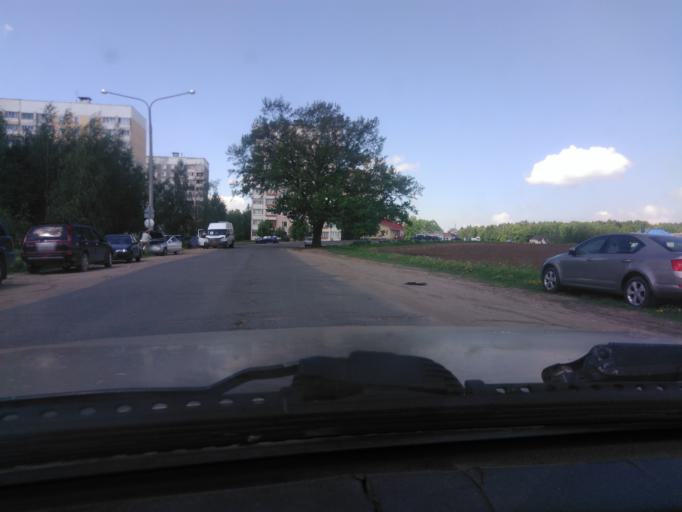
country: BY
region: Mogilev
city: Palykavichy Pyershyya
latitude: 53.9500
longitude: 30.3737
